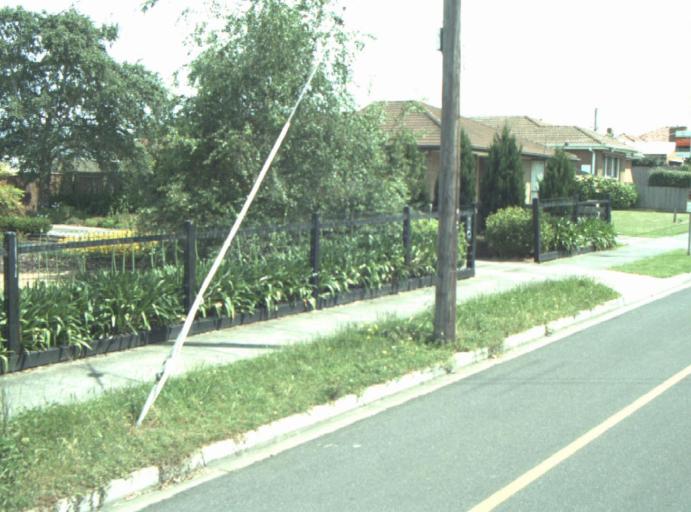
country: AU
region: Victoria
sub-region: Greater Geelong
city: Clifton Springs
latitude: -38.1698
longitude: 144.5715
